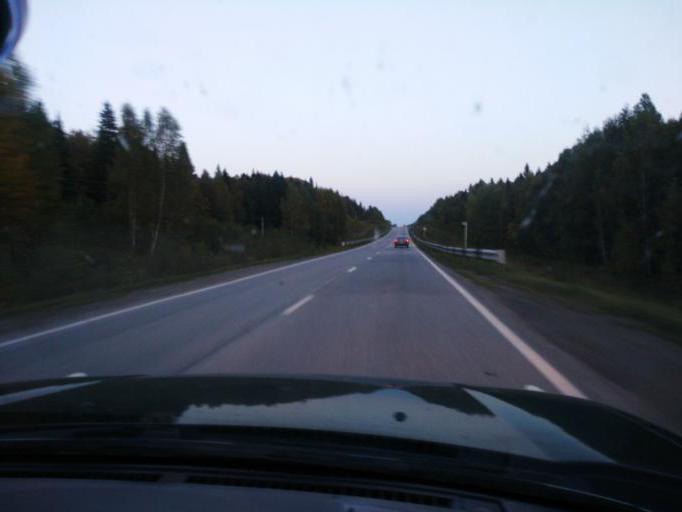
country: RU
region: Perm
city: Verkhnechusovskiye Gorodki
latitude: 58.2726
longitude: 56.9448
